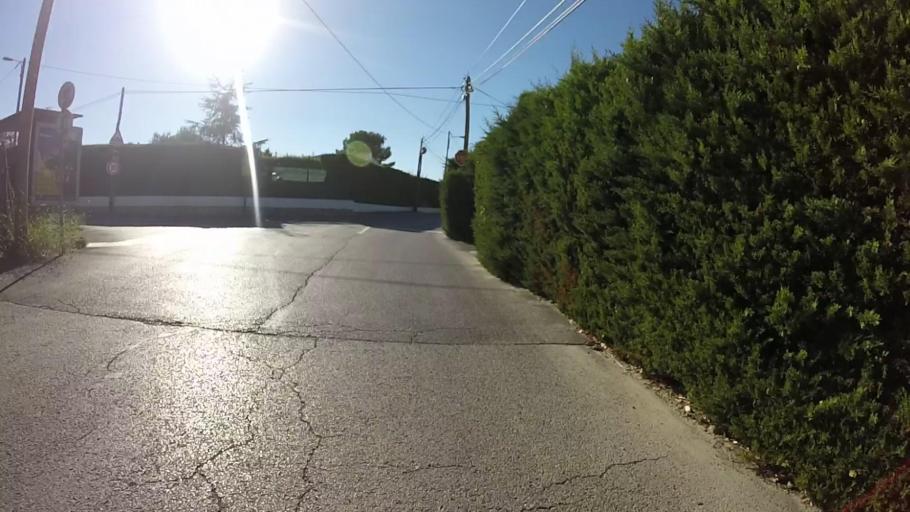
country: FR
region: Provence-Alpes-Cote d'Azur
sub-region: Departement des Alpes-Maritimes
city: Mougins
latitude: 43.6102
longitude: 7.0069
